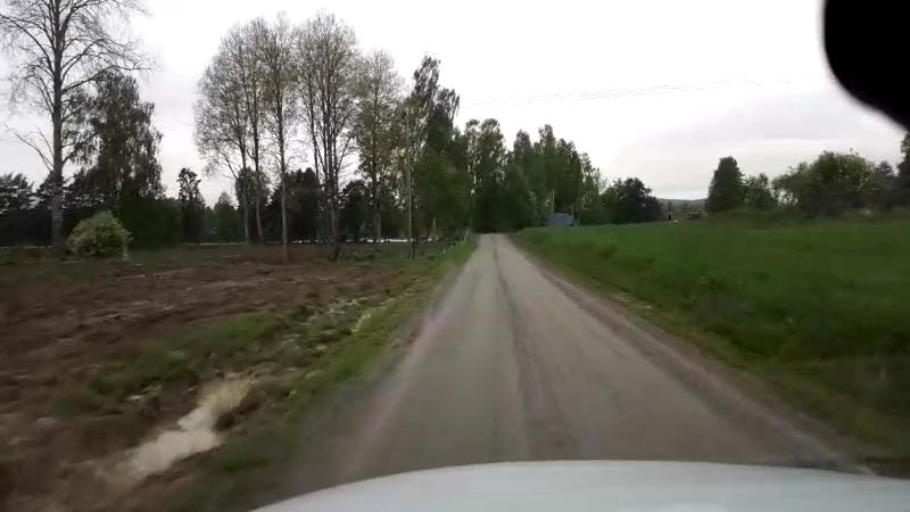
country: SE
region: Gaevleborg
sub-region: Ljusdals Kommun
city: Jaervsoe
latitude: 61.7619
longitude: 16.1735
